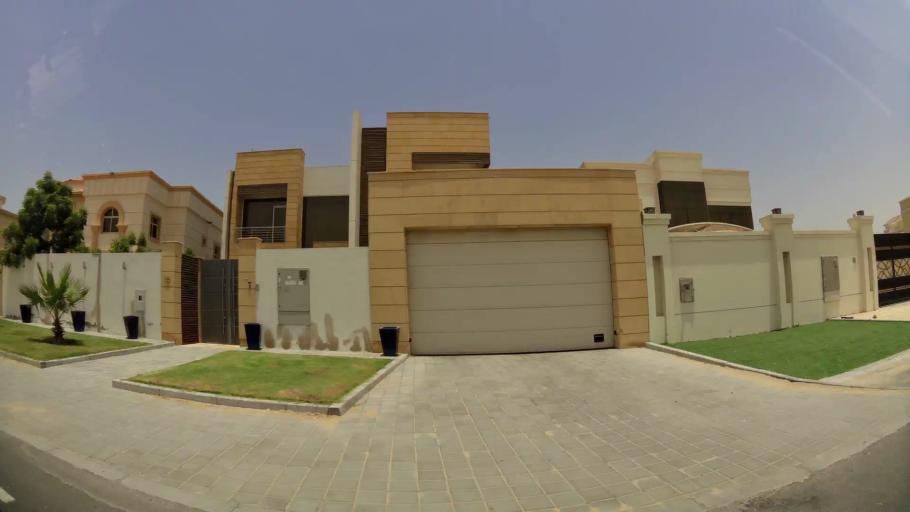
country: AE
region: Dubai
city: Dubai
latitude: 25.0913
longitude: 55.2283
